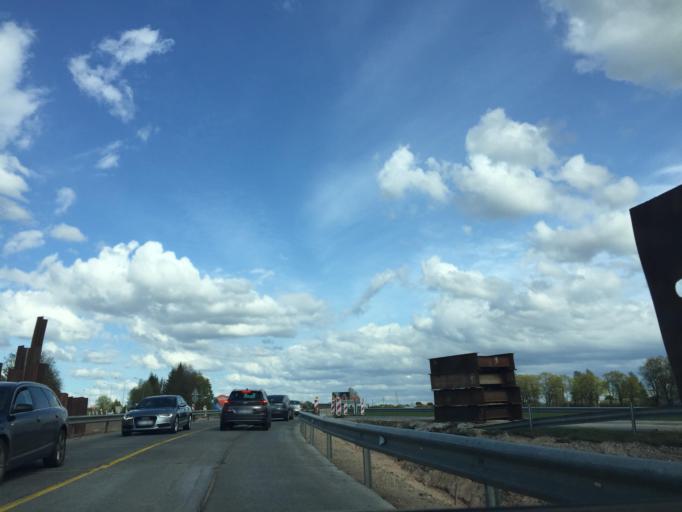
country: LV
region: Sigulda
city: Sigulda
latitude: 57.1410
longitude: 24.8353
